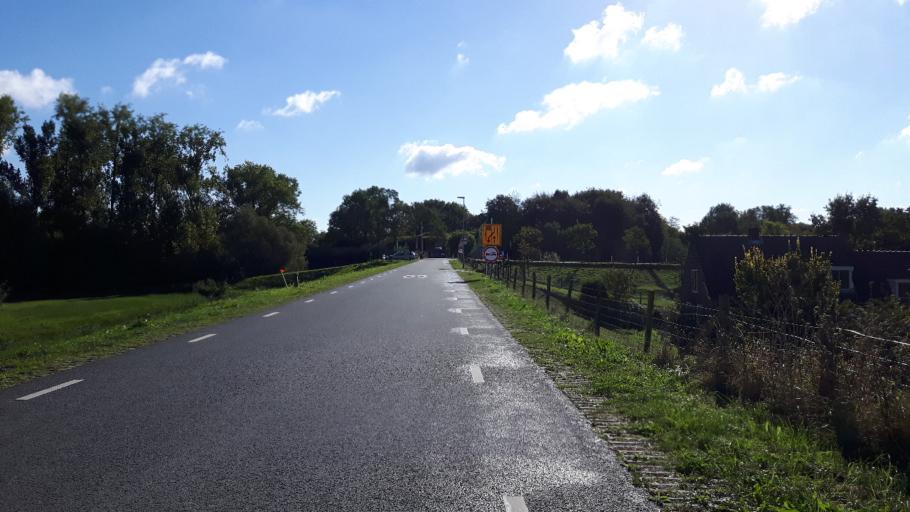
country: NL
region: Gelderland
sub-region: Gemeente Culemborg
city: Culemborg
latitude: 51.9635
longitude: 5.1718
